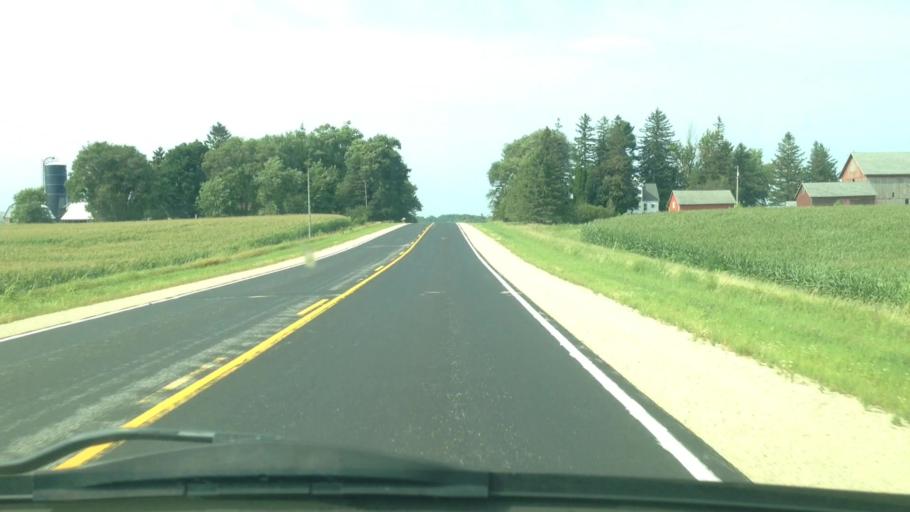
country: US
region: Minnesota
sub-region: Winona County
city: Lewiston
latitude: 43.9064
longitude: -91.9594
